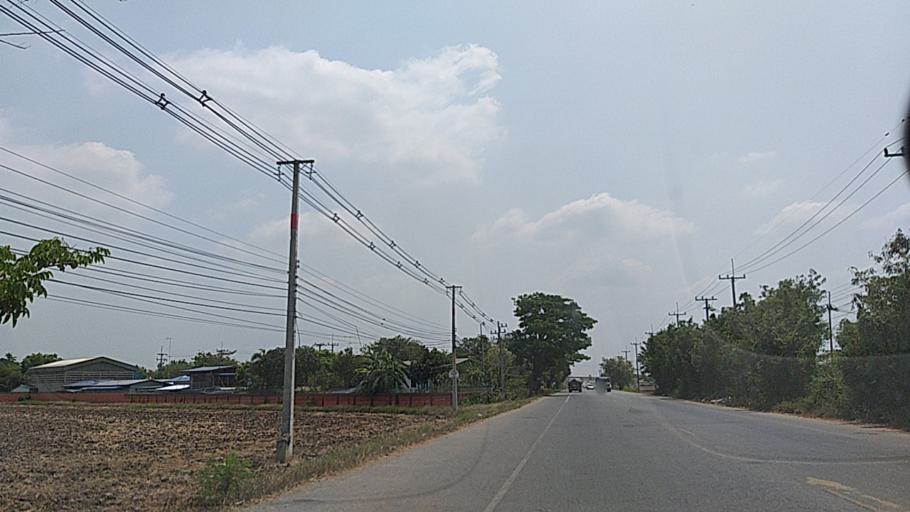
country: TH
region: Chachoengsao
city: Chachoengsao
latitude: 13.7532
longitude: 101.0763
